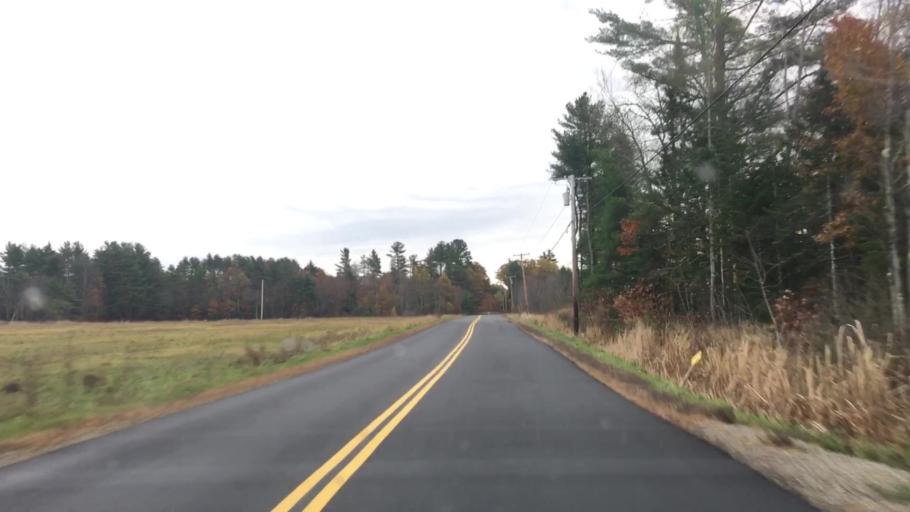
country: US
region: Maine
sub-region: Kennebec County
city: Pittston
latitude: 44.1685
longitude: -69.7109
